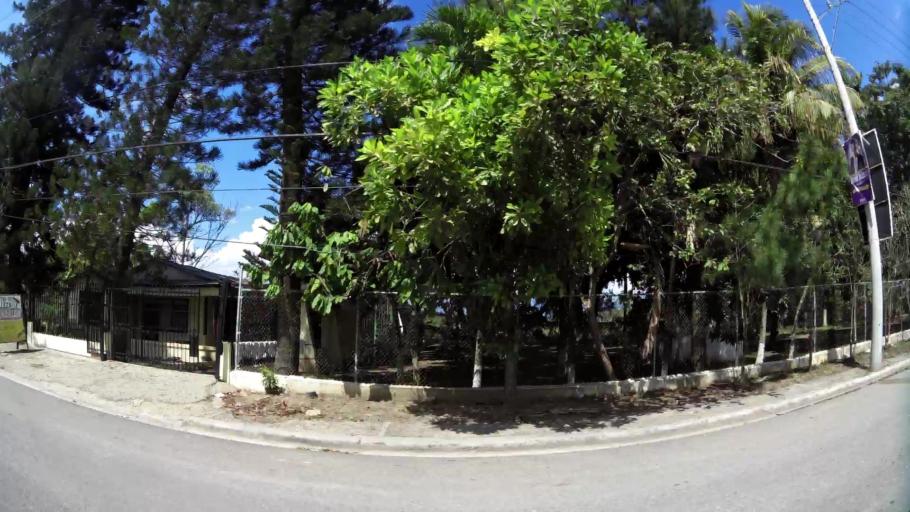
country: DO
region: Santiago
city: Licey al Medio
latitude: 19.3824
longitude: -70.6200
